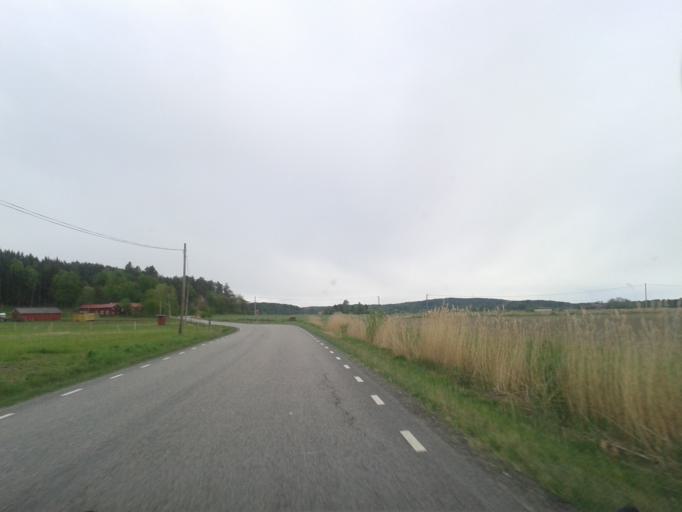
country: SE
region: Vaestra Goetaland
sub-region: Kungalvs Kommun
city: Kode
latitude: 57.9634
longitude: 11.8213
